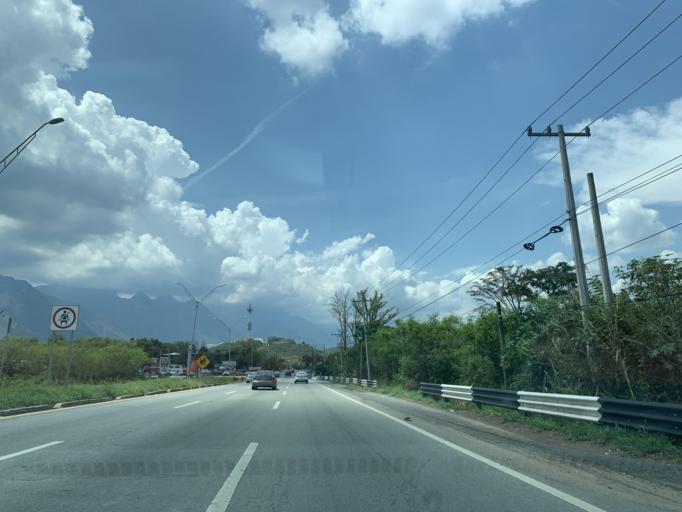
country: MX
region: Nuevo Leon
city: Santiago
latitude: 25.3970
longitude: -100.1250
